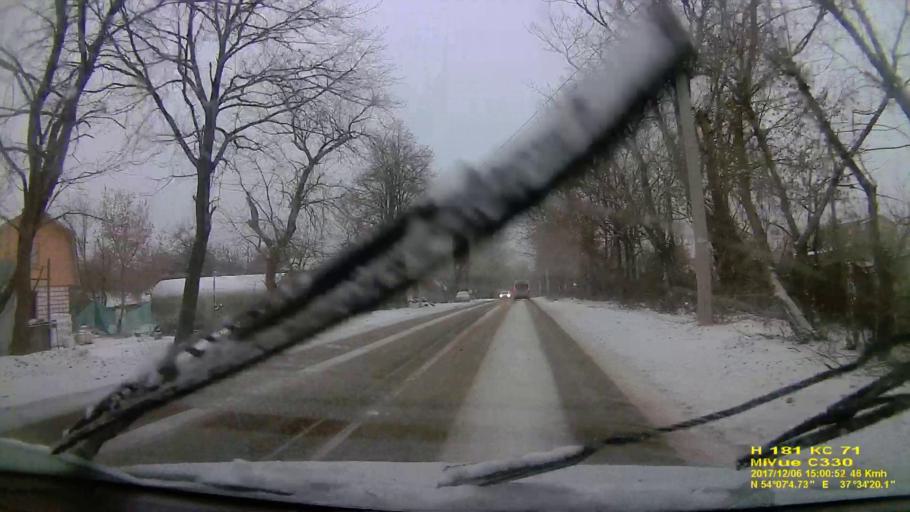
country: RU
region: Tula
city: Mendeleyevskiy
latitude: 54.1180
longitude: 37.5722
